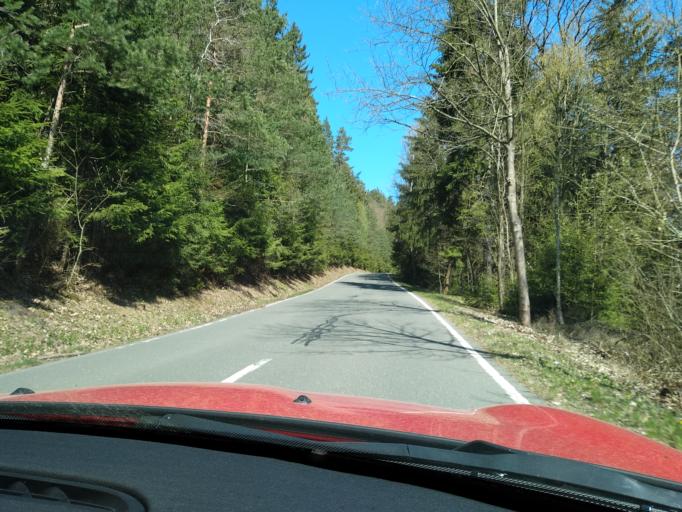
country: DE
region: Thuringia
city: Bad Blankenburg
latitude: 50.6456
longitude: 11.2821
